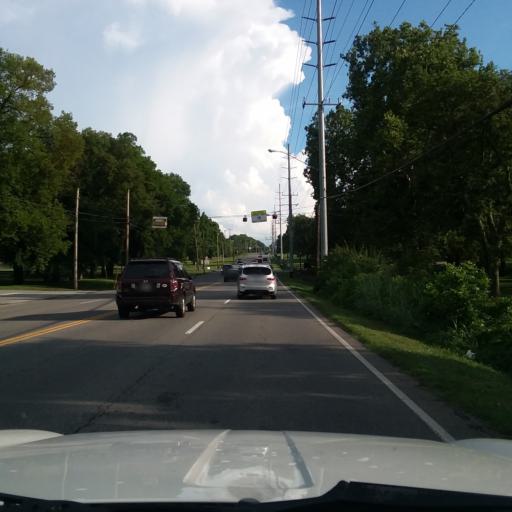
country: US
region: Tennessee
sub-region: Davidson County
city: Oak Hill
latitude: 36.0816
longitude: -86.7727
